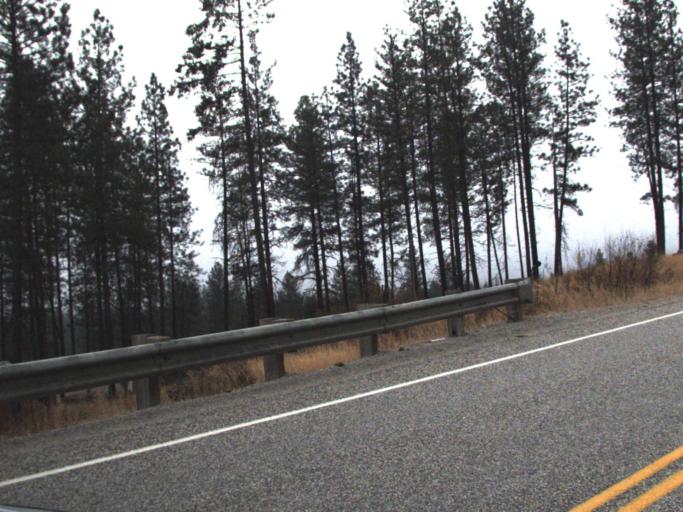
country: US
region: Washington
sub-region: Stevens County
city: Kettle Falls
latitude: 48.7537
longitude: -118.1345
